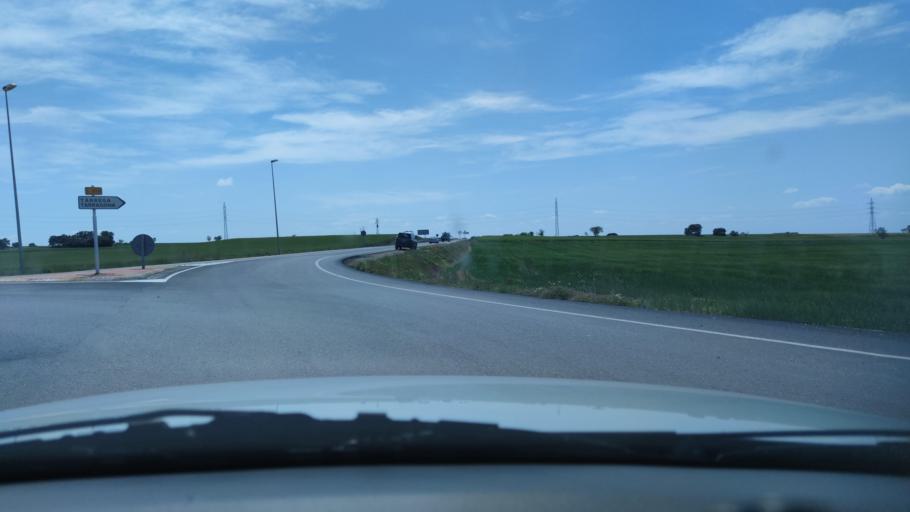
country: ES
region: Catalonia
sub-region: Provincia de Lleida
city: Mont-roig del Camp
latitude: 41.7256
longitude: 1.2045
